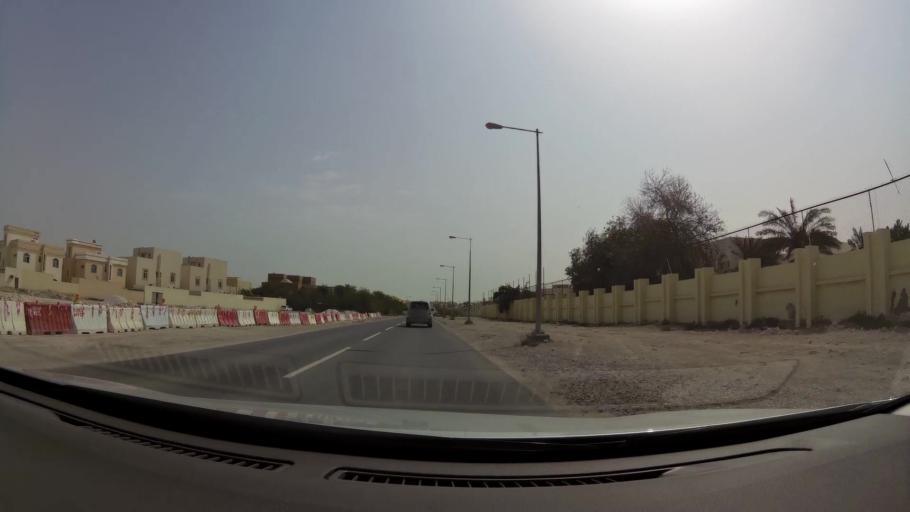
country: QA
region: Baladiyat ad Dawhah
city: Doha
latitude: 25.3028
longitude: 51.4776
